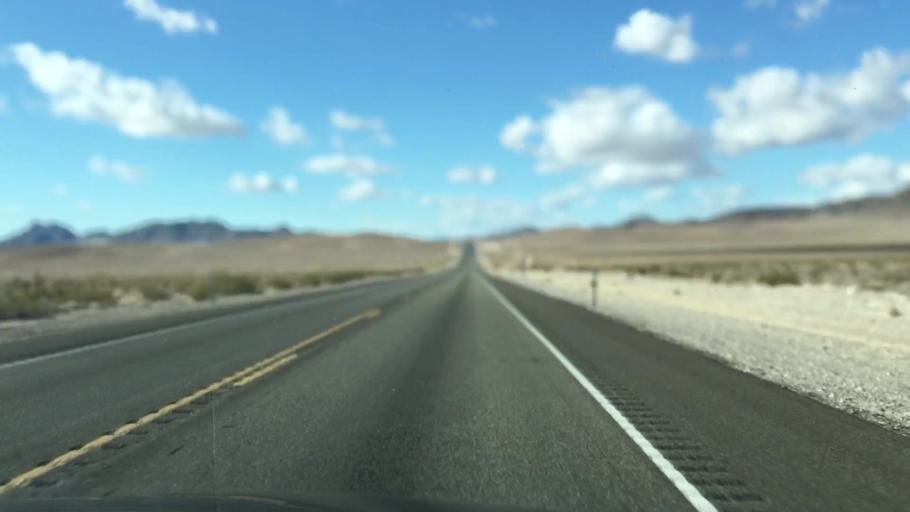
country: US
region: Nevada
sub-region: Nye County
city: Pahrump
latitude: 36.6057
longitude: -116.2593
